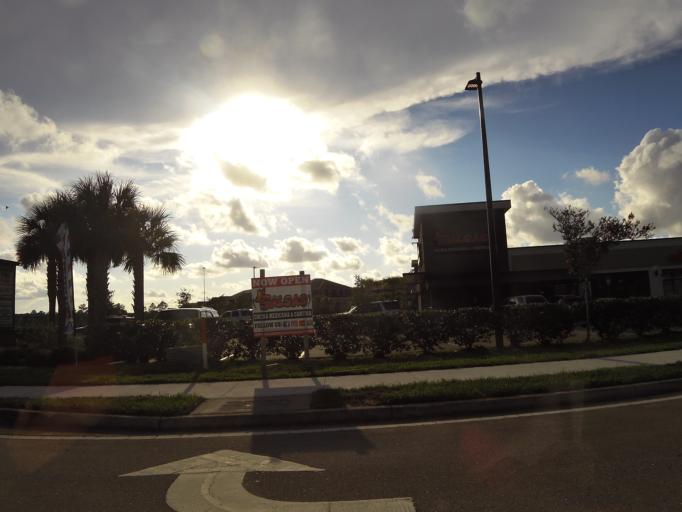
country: US
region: Florida
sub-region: Saint Johns County
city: Ponte Vedra Beach
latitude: 30.2175
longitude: -81.5097
